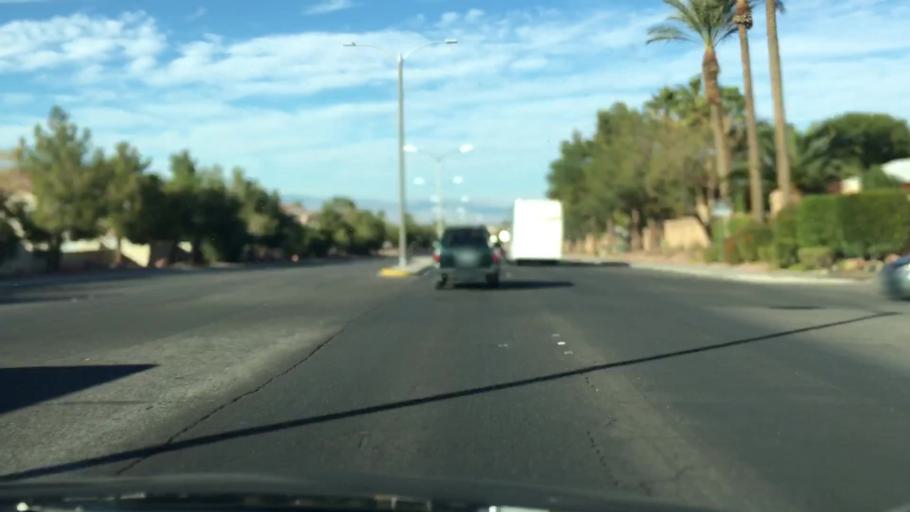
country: US
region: Nevada
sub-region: Clark County
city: Whitney
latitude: 36.0292
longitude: -115.1004
